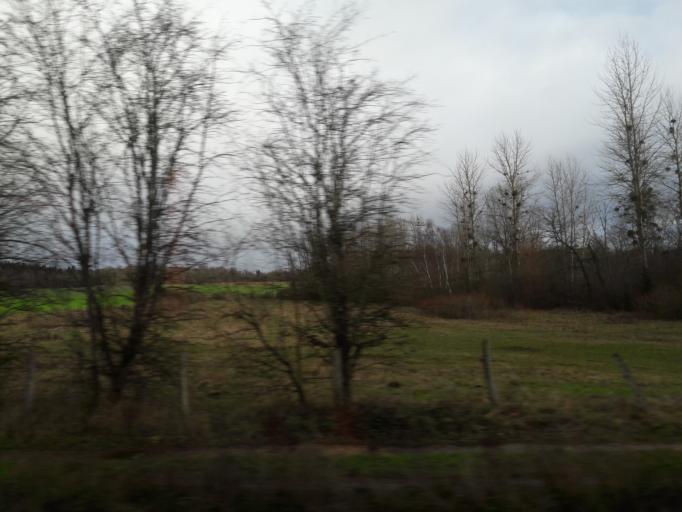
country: FR
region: Franche-Comte
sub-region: Territoire de Belfort
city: Grandvillars
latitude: 47.5452
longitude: 6.9552
